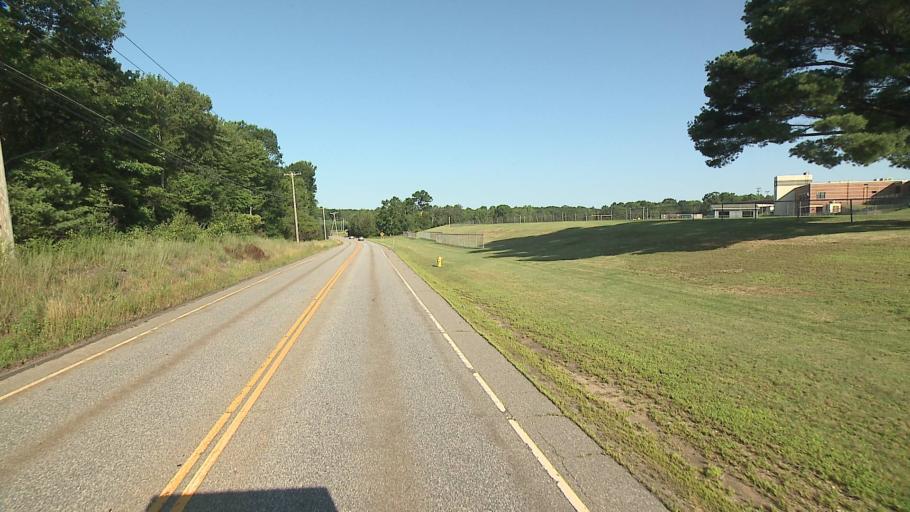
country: US
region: Connecticut
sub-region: Hartford County
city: Collinsville
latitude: 41.7780
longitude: -72.9875
